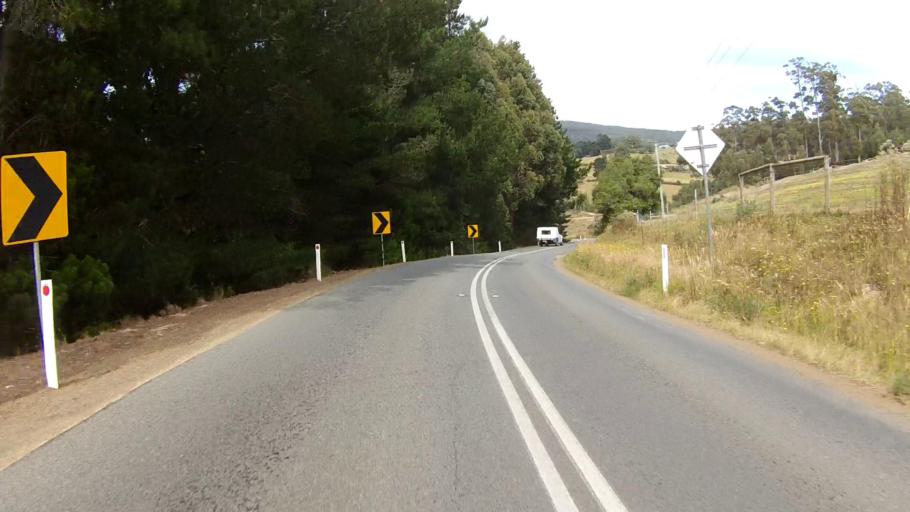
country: AU
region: Tasmania
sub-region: Kingborough
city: Kettering
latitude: -43.1747
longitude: 147.2373
